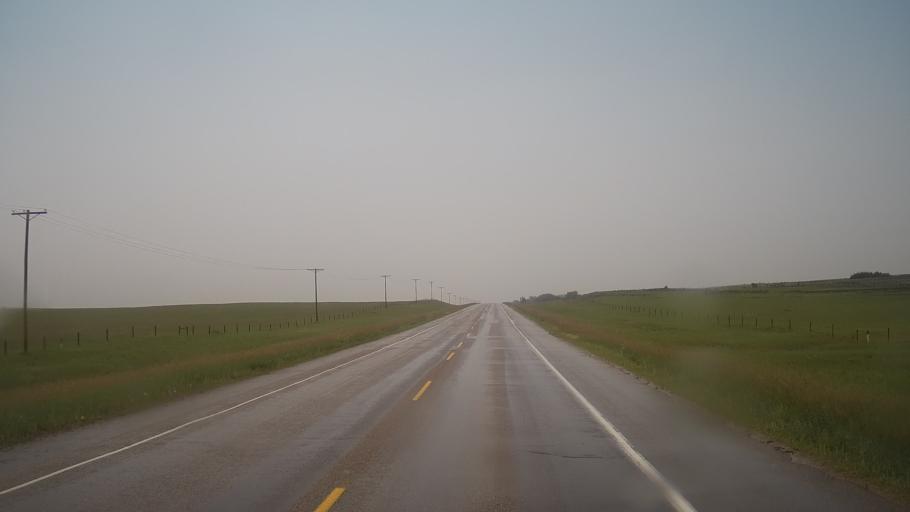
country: CA
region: Saskatchewan
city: Biggar
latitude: 52.0820
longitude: -108.0343
